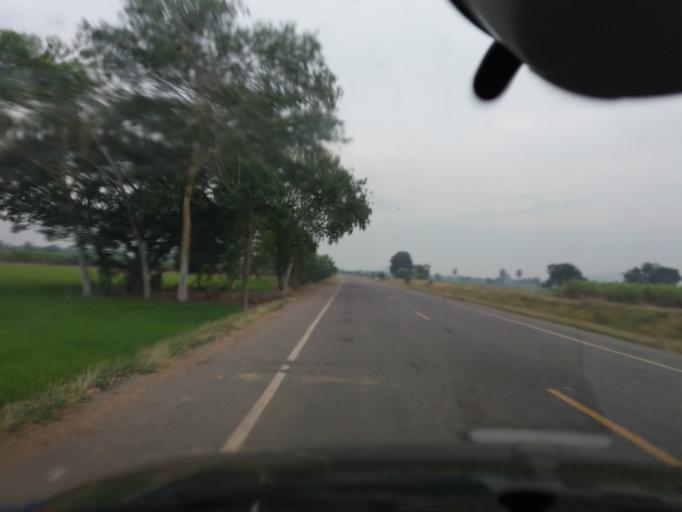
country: TH
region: Suphan Buri
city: Doem Bang Nang Buat
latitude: 14.8638
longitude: 100.1301
